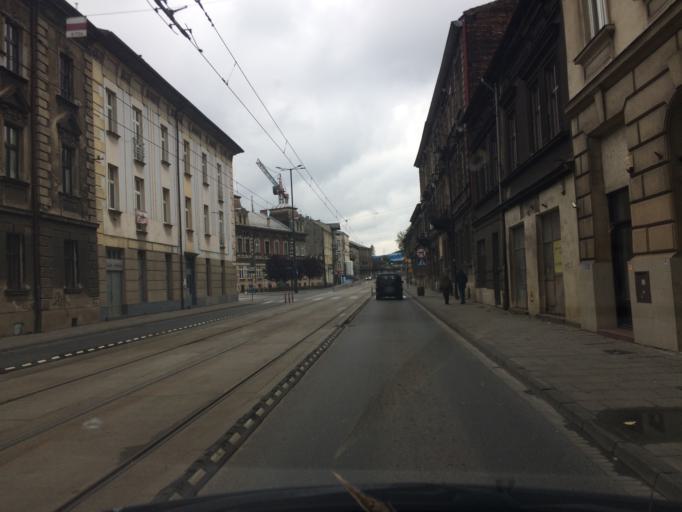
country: PL
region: Lesser Poland Voivodeship
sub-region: Krakow
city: Krakow
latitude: 50.0445
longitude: 19.9571
